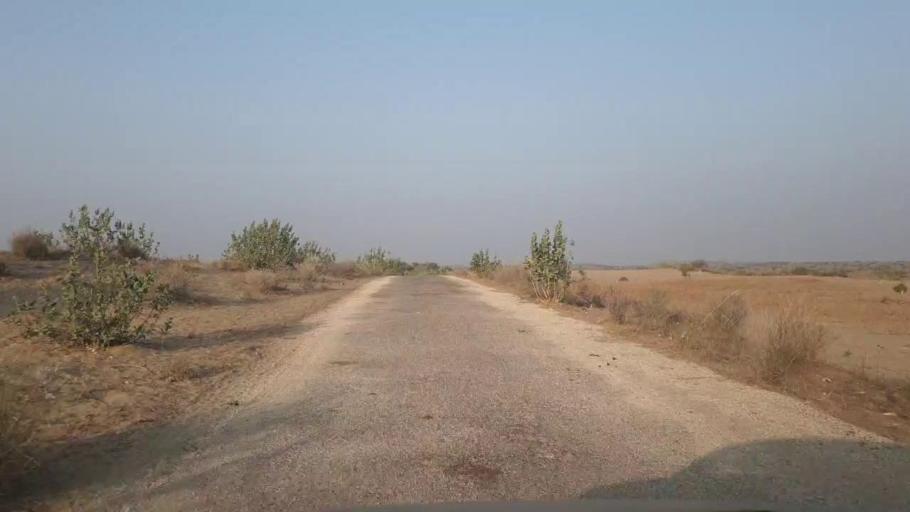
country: PK
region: Sindh
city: Umarkot
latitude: 25.2444
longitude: 69.8973
